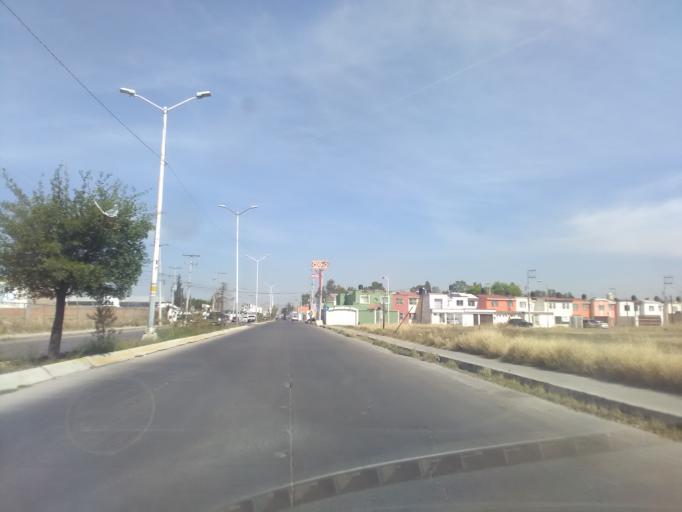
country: MX
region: Durango
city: Victoria de Durango
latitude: 24.0488
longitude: -104.6248
